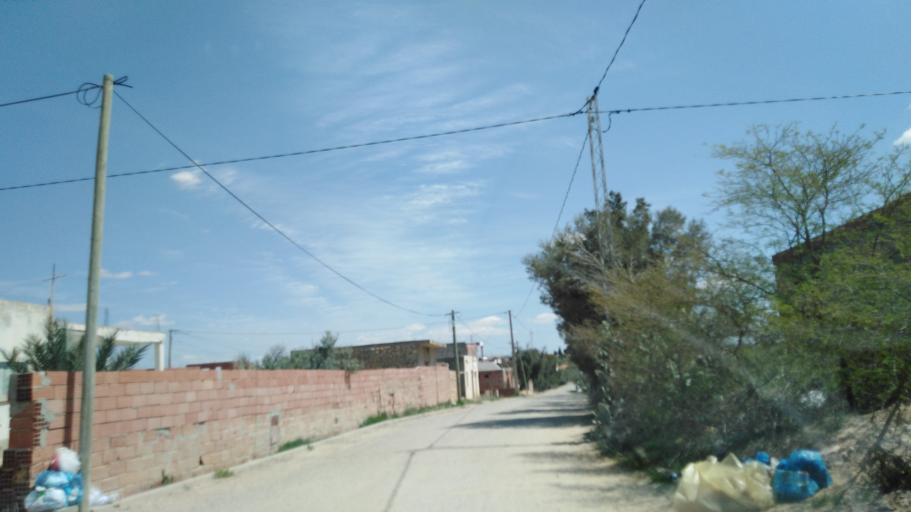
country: TN
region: Safaqis
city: Sfax
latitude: 34.7426
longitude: 10.5447
